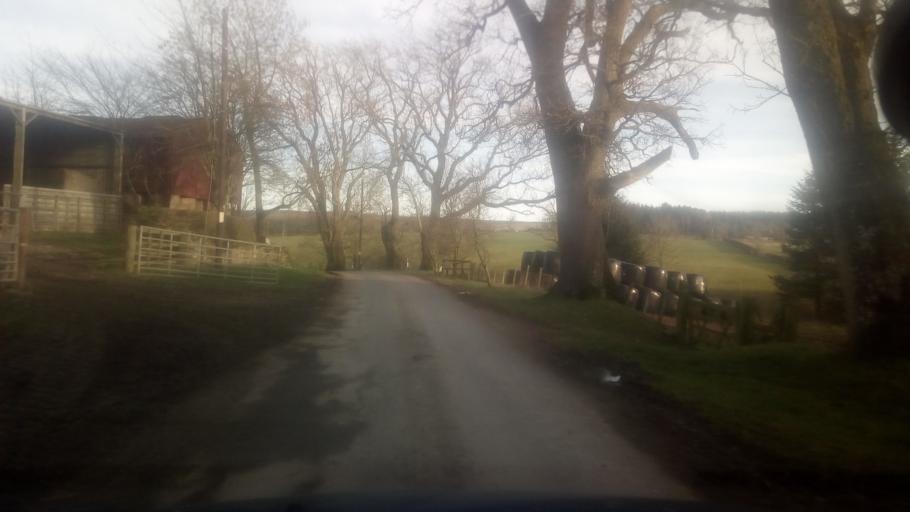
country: GB
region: Scotland
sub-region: The Scottish Borders
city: Jedburgh
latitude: 55.4087
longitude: -2.6062
